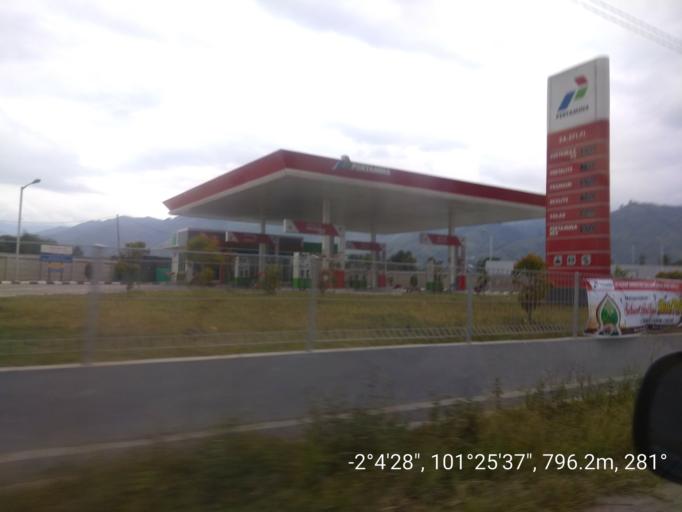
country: ID
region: Jambi
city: Sungai Penuh
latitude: -2.0745
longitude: 101.4269
